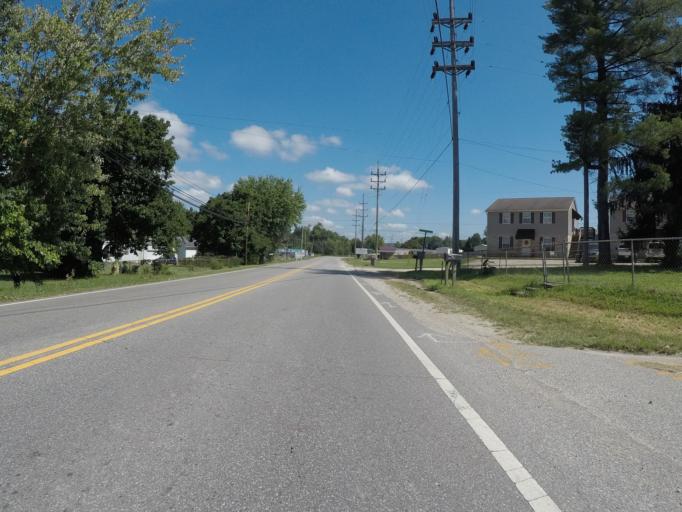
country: US
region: Ohio
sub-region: Lawrence County
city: Burlington
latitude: 38.4101
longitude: -82.5197
